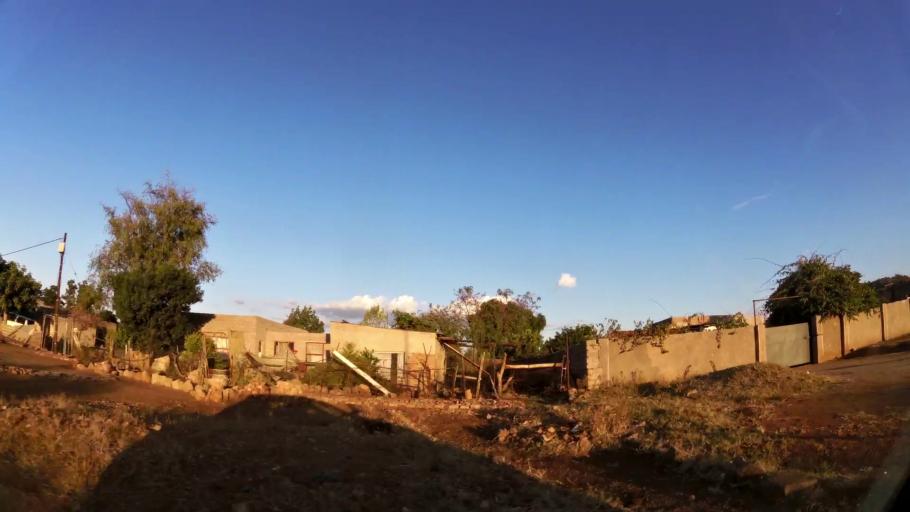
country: ZA
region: Limpopo
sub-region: Waterberg District Municipality
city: Mokopane
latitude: -24.1456
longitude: 28.9724
